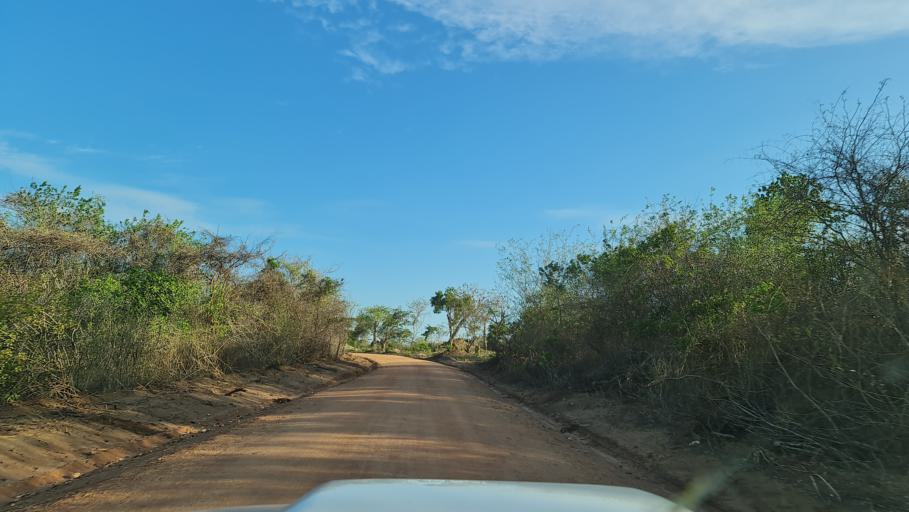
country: MZ
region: Nampula
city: Nacala
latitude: -14.6916
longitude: 40.3167
